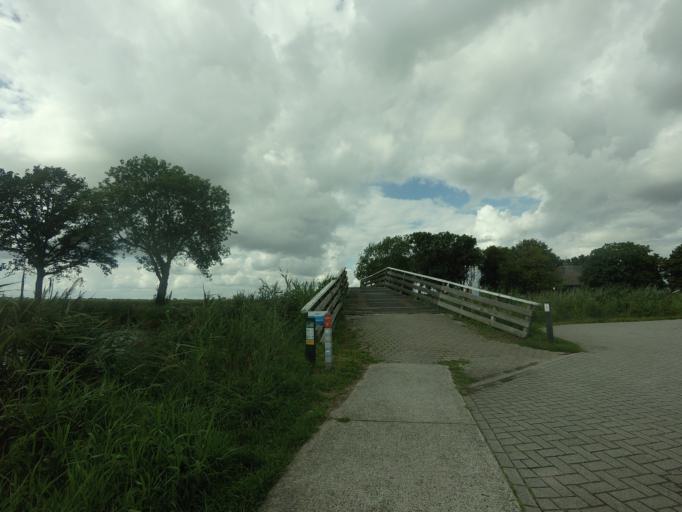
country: NL
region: Overijssel
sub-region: Gemeente Steenwijkerland
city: Giethoorn
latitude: 52.7391
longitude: 6.0519
